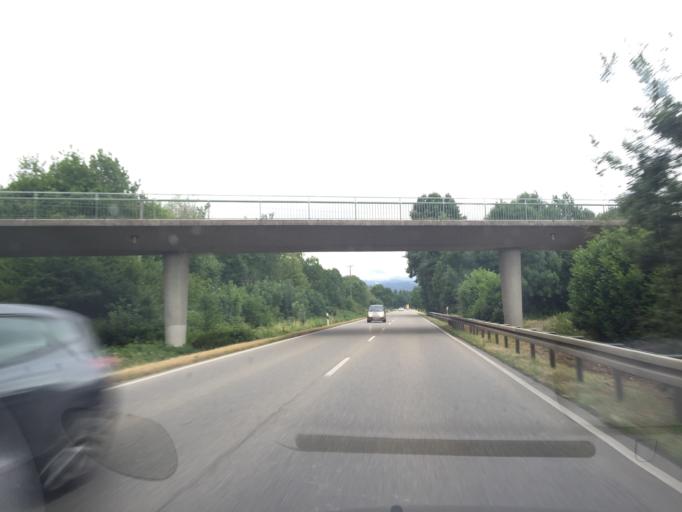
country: DE
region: Baden-Wuerttemberg
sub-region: Freiburg Region
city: Unterkrozingen
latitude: 47.9352
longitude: 7.6858
